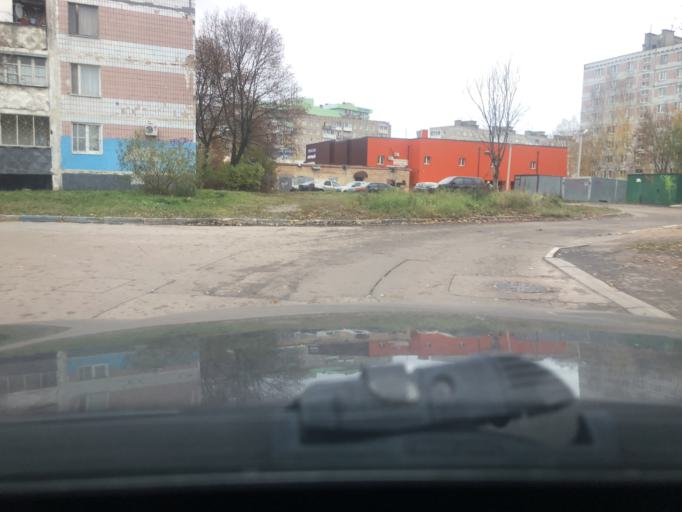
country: RU
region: Moskovskaya
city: Sergiyev Posad
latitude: 56.3230
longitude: 38.1331
